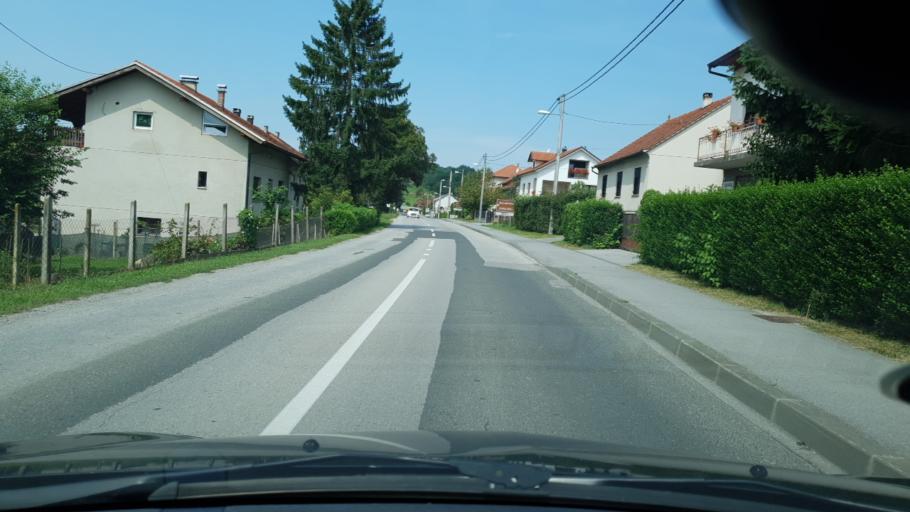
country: HR
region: Krapinsko-Zagorska
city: Bedekovcina
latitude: 46.0401
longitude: 15.9875
